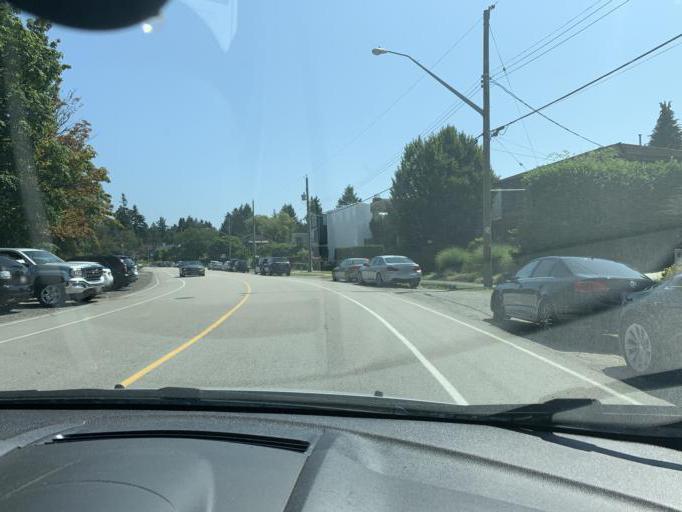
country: CA
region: British Columbia
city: West End
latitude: 49.2745
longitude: -123.2103
